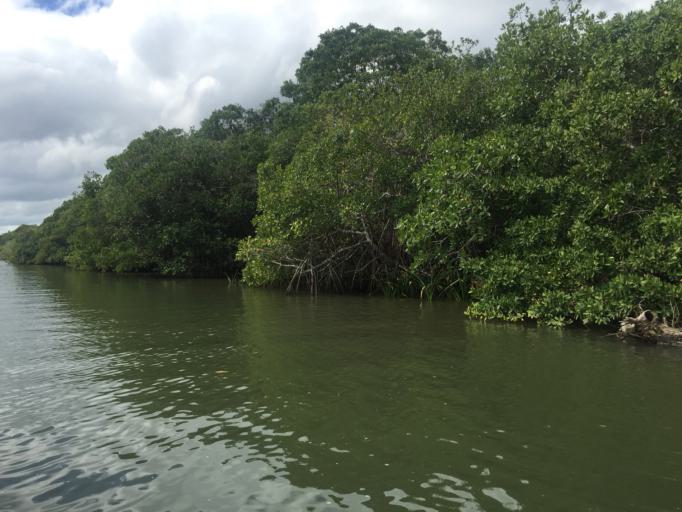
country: MX
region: Veracruz
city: Tecolutla
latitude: 20.4677
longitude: -97.0082
